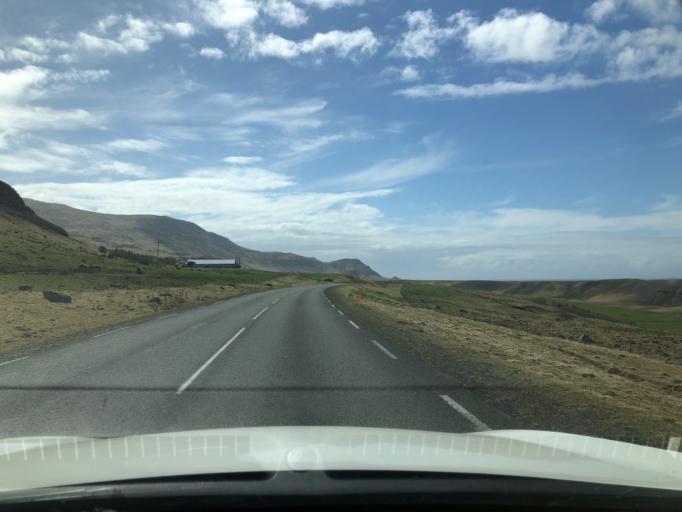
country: IS
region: Capital Region
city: Mosfellsbaer
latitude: 64.3111
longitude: -21.7715
